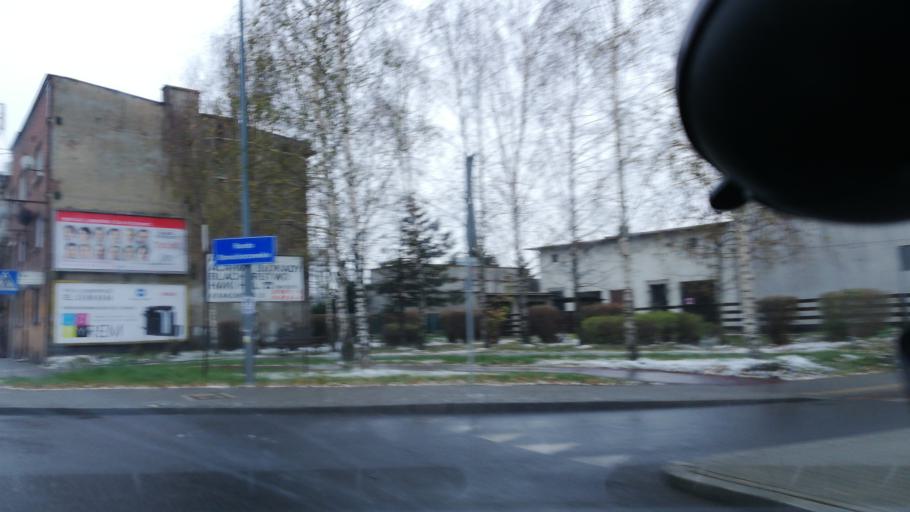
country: PL
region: Silesian Voivodeship
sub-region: Chorzow
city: Chorzow
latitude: 50.3002
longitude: 18.9704
